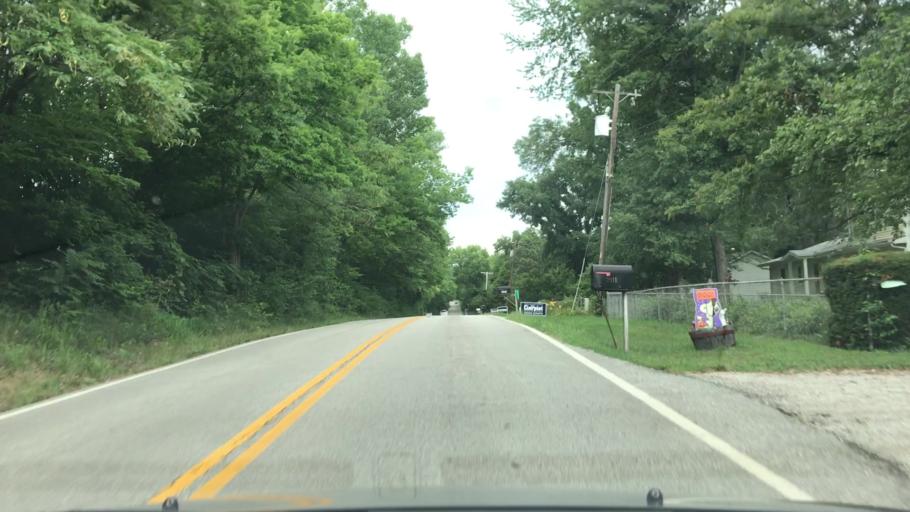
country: US
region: Missouri
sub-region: Jackson County
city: Lees Summit
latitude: 38.8910
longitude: -94.4413
